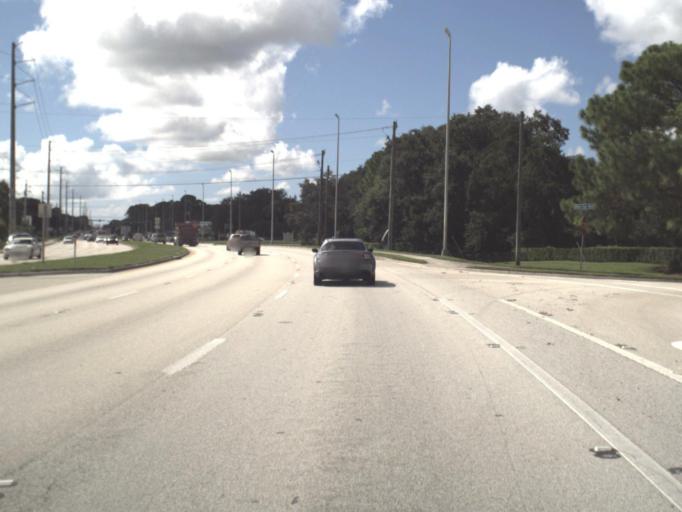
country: US
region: Florida
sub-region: Manatee County
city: Samoset
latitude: 27.4471
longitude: -82.5117
